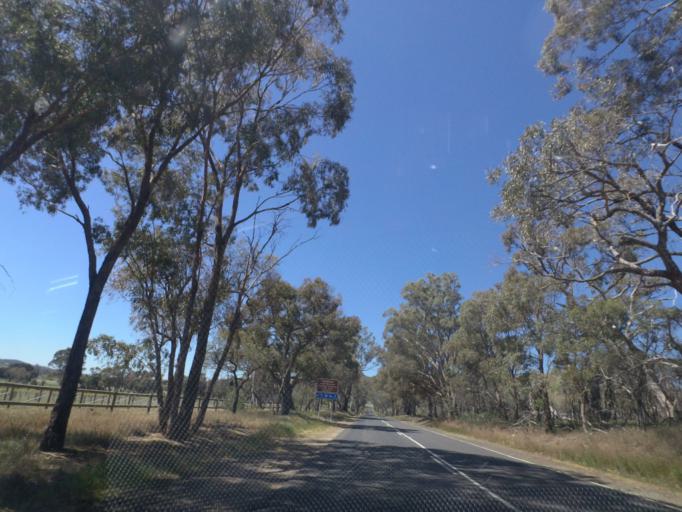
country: AU
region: Victoria
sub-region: Hume
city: Sunbury
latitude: -37.0505
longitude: 144.7919
